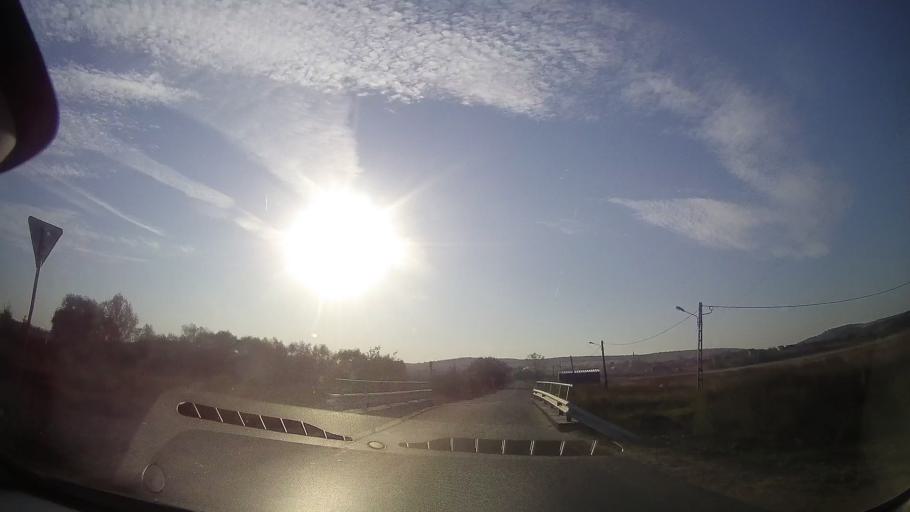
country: RO
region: Timis
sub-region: Comuna Masloc
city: Masloc
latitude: 45.9725
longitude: 21.4717
